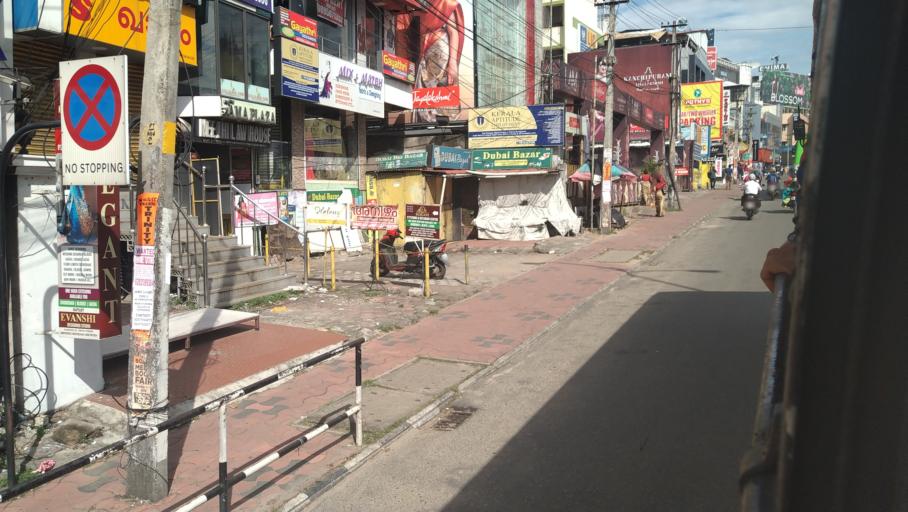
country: IN
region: Kerala
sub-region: Thiruvananthapuram
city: Thiruvananthapuram
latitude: 8.4884
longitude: 76.9474
